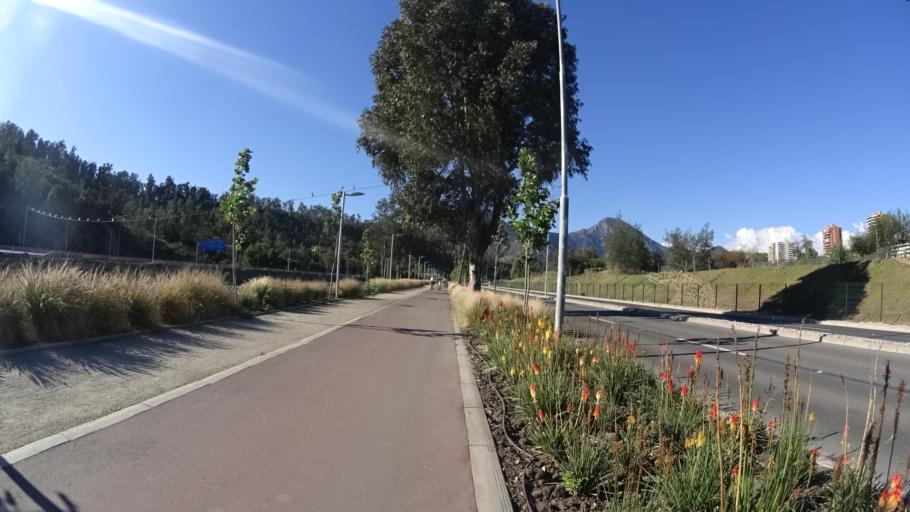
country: CL
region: Santiago Metropolitan
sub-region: Provincia de Santiago
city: Villa Presidente Frei, Nunoa, Santiago, Chile
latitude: -33.3991
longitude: -70.6034
